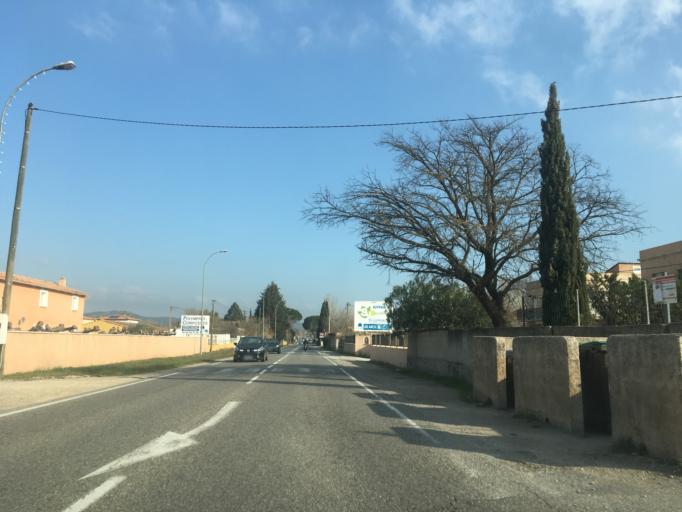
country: FR
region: Provence-Alpes-Cote d'Azur
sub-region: Departement du Var
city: Vidauban
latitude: 43.4158
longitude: 6.4203
